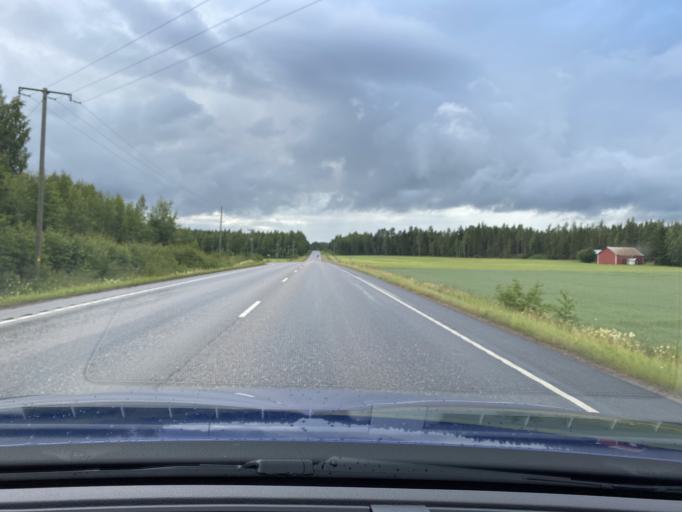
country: FI
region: Uusimaa
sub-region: Helsinki
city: Nurmijaervi
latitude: 60.5499
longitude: 24.8272
